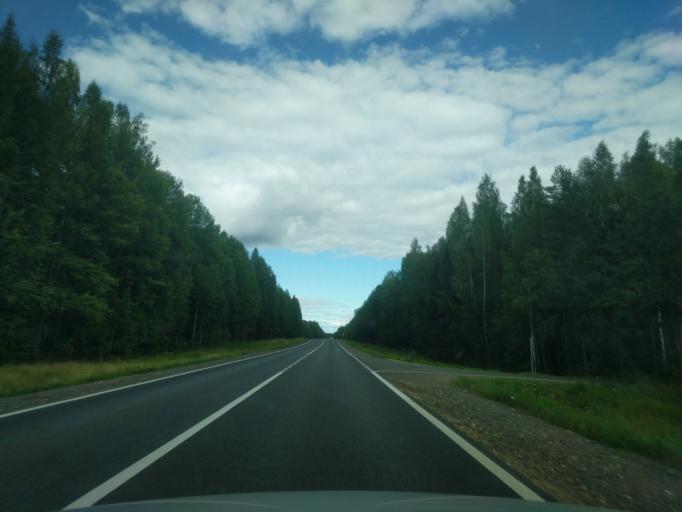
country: RU
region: Kostroma
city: Kadyy
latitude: 57.8432
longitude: 43.4506
